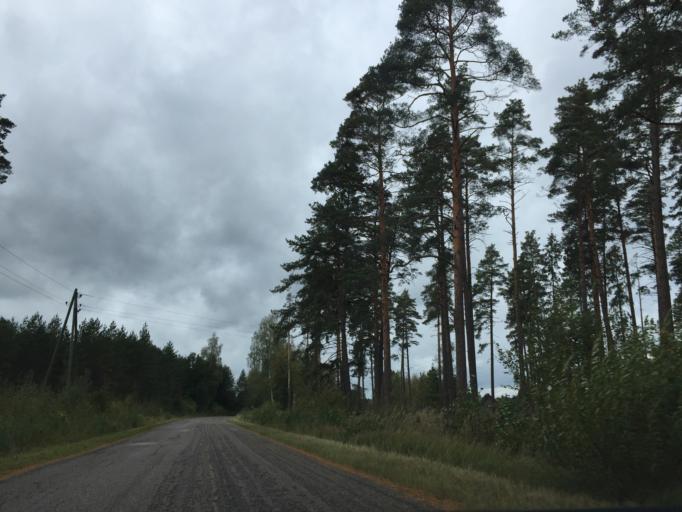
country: LV
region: Olaine
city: Olaine
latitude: 56.7652
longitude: 23.8862
